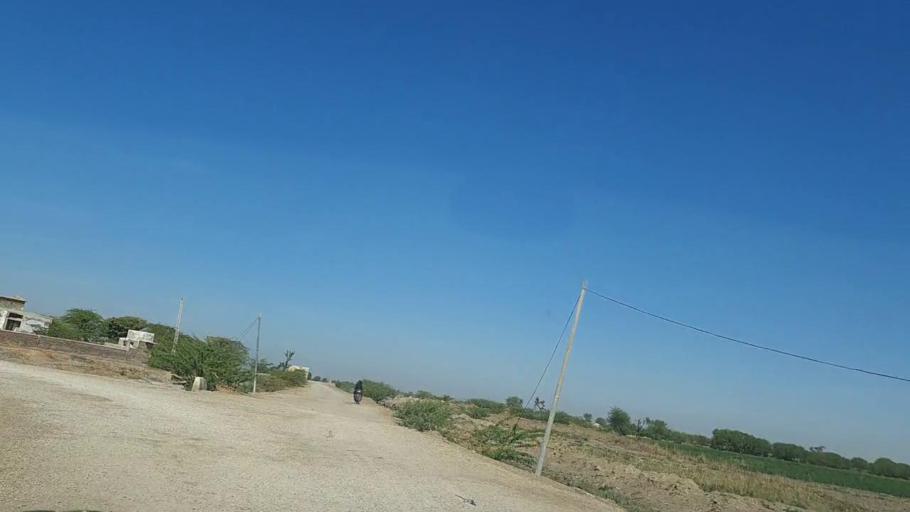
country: PK
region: Sindh
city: Dhoro Naro
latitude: 25.4862
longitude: 69.5272
